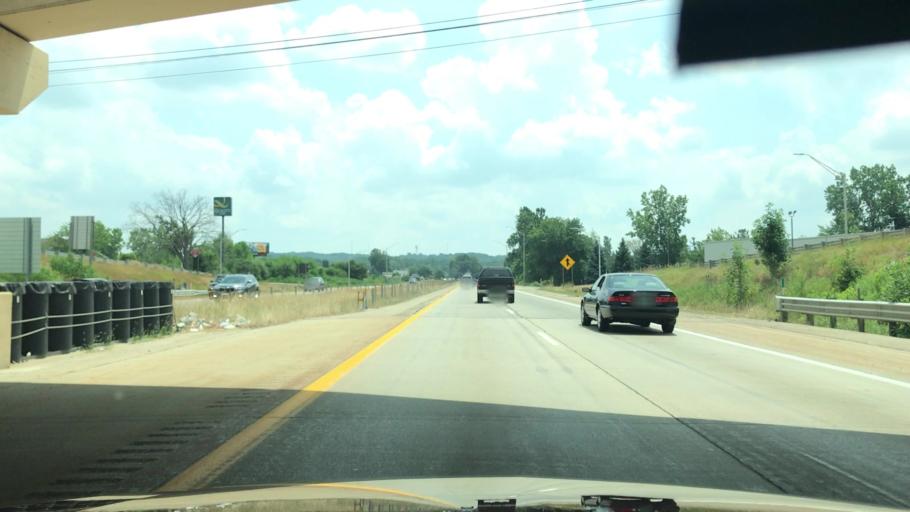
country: US
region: Michigan
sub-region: Kent County
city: Cutlerville
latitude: 42.8263
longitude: -85.6721
